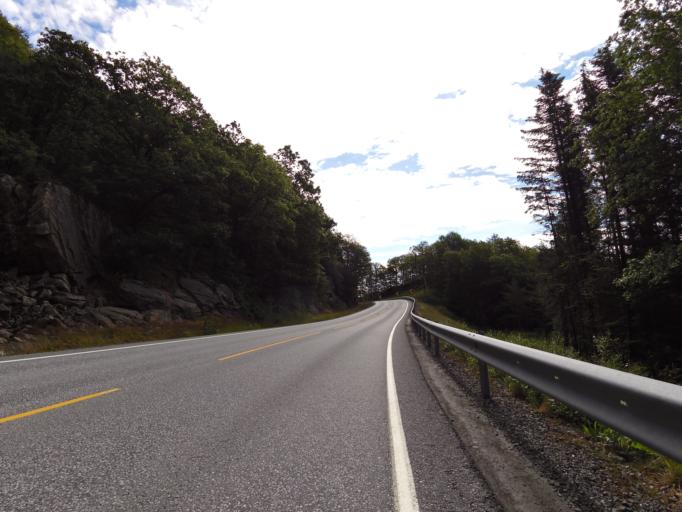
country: NO
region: Vest-Agder
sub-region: Lyngdal
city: Lyngdal
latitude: 58.0494
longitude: 7.1716
